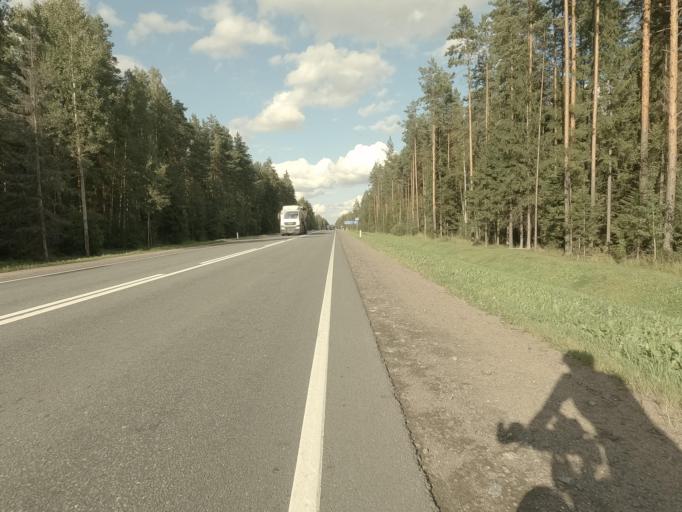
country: RU
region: Leningrad
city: Mga
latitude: 59.6917
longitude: 30.9768
